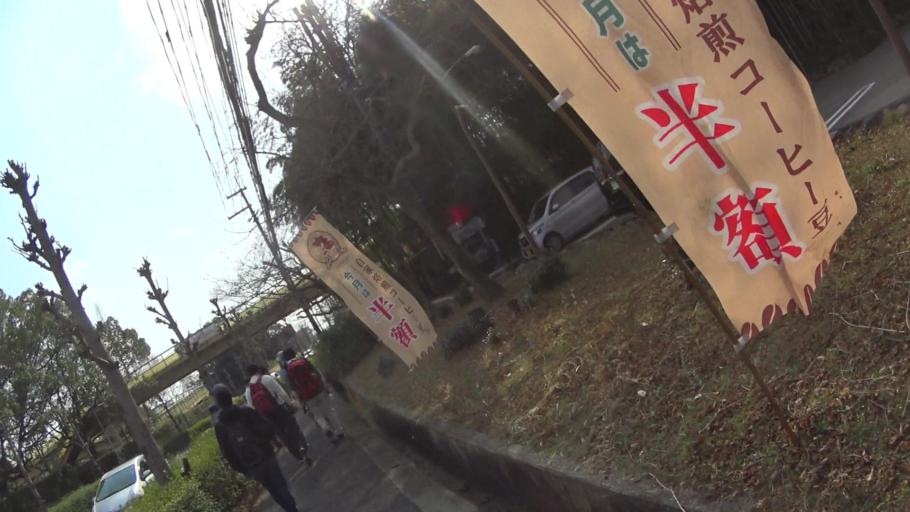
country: JP
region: Nara
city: Nara-shi
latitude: 34.6981
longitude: 135.8277
